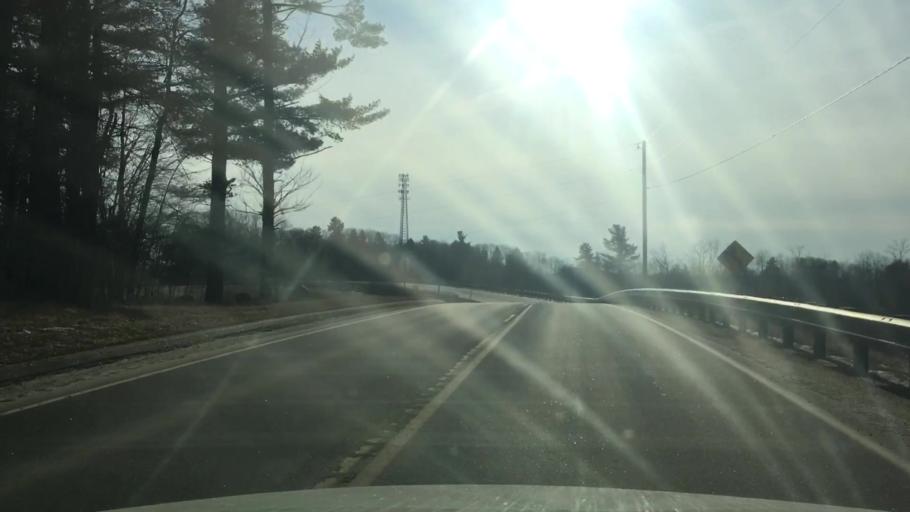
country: US
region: Maine
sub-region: Androscoggin County
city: Sabattus
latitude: 44.1185
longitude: -70.0870
